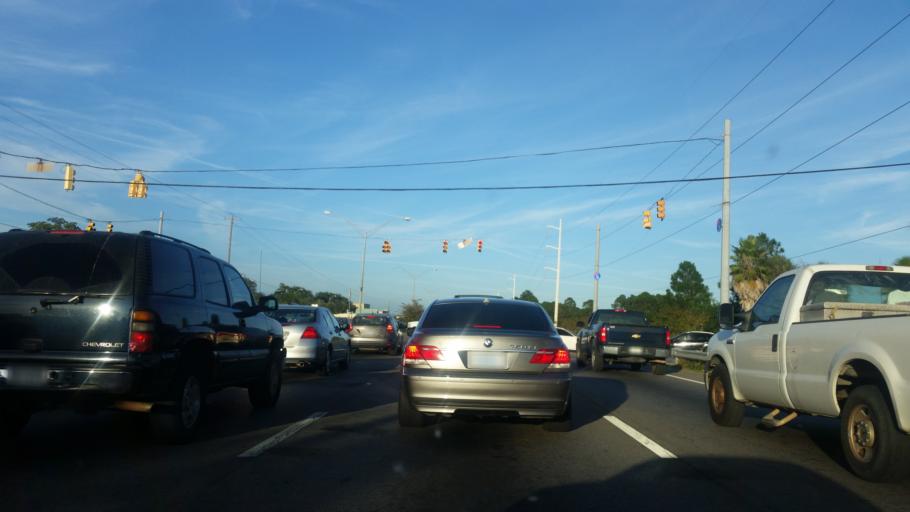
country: US
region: Mississippi
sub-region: Jackson County
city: Pascagoula
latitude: 30.3729
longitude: -88.5350
